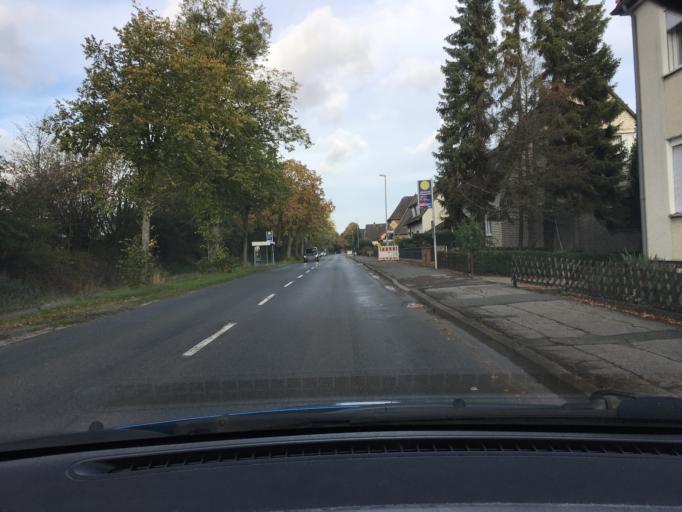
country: DE
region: Lower Saxony
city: Barsinghausen
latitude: 52.3144
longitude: 9.4386
